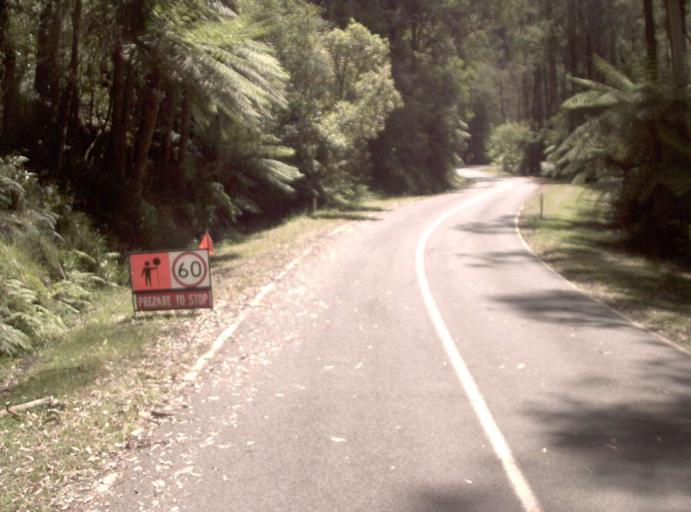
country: AU
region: Victoria
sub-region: Yarra Ranges
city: Millgrove
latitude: -37.7163
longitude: 145.7151
